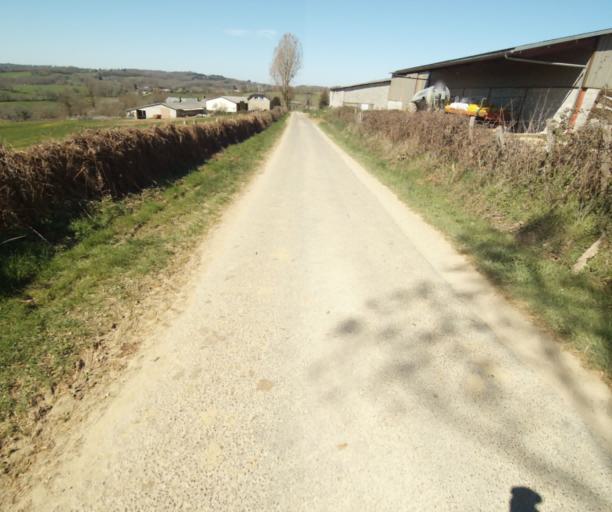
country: FR
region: Limousin
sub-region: Departement de la Correze
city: Chamboulive
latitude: 45.4460
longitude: 1.6775
